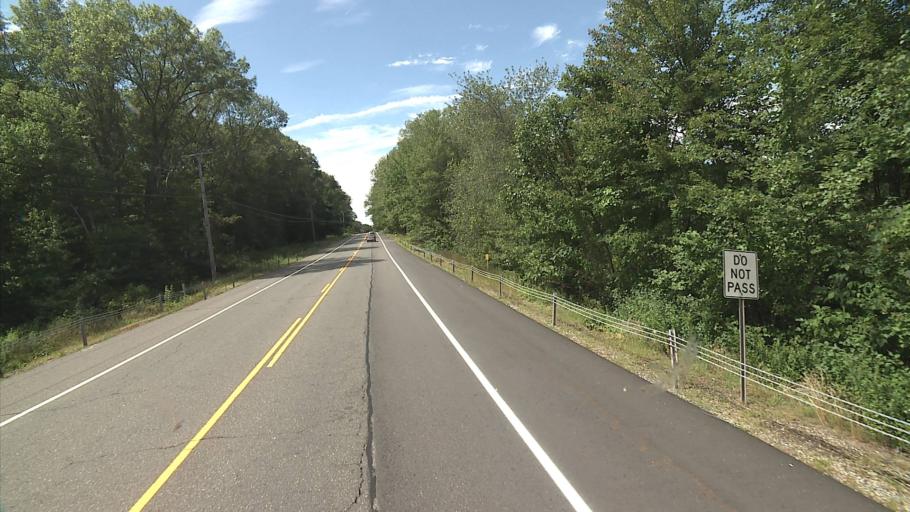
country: US
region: Connecticut
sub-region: Tolland County
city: Storrs
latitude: 41.8301
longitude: -72.2780
